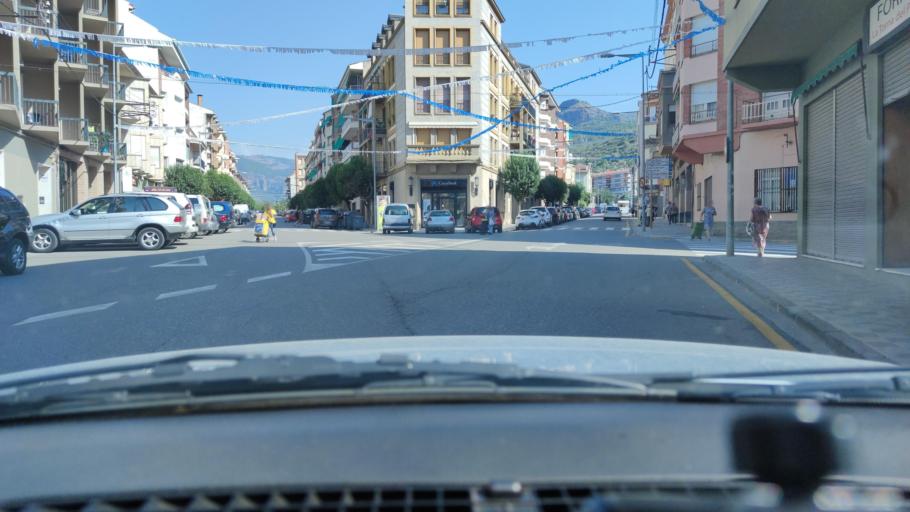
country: ES
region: Catalonia
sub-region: Provincia de Lleida
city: Senterada
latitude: 42.2485
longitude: 0.9665
